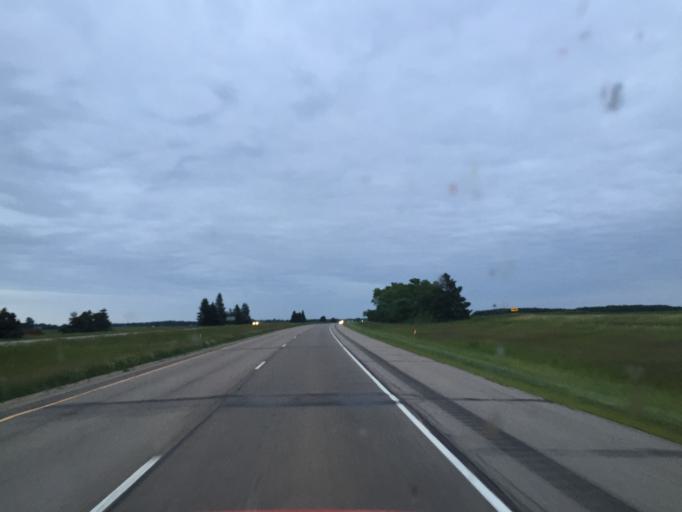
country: US
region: Minnesota
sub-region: Mower County
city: Austin
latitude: 43.6598
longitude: -93.0705
